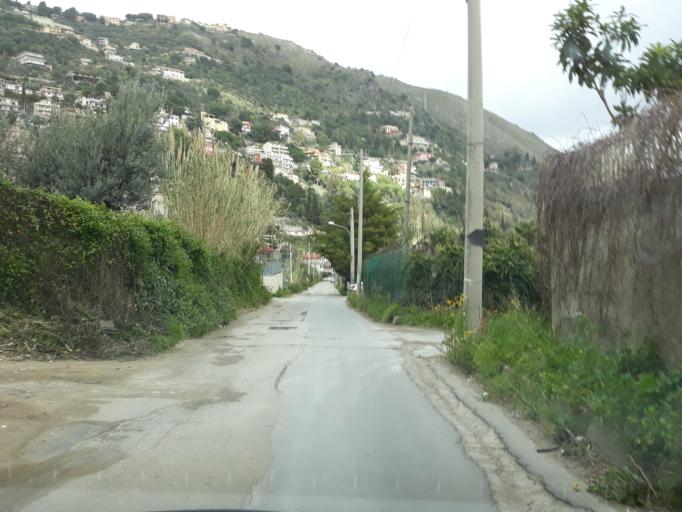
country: IT
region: Sicily
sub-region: Palermo
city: Monreale
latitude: 38.0832
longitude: 13.2980
